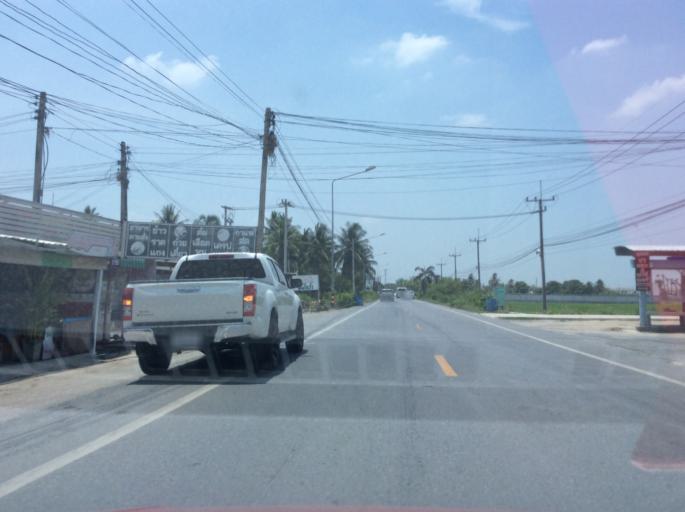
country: TH
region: Pathum Thani
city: Ban Lam Luk Ka
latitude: 13.9900
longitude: 100.7778
